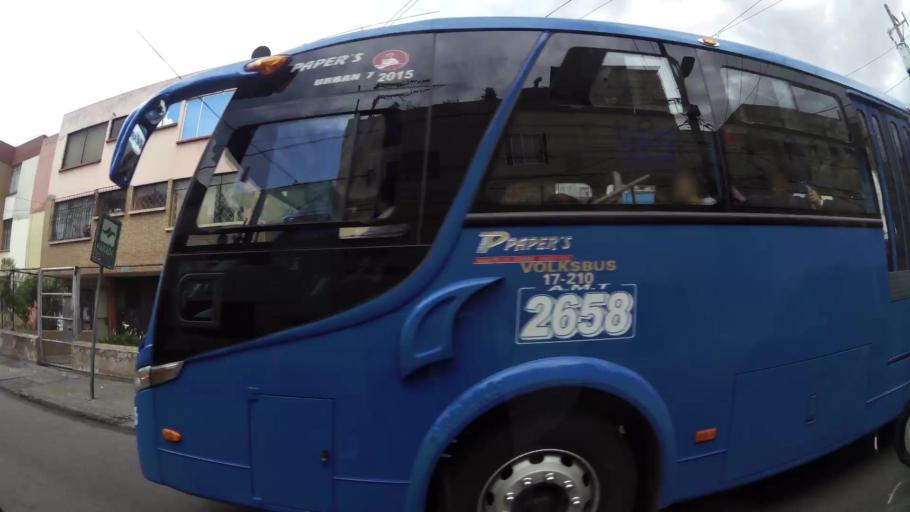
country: EC
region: Pichincha
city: Quito
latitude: -0.2672
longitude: -78.5424
